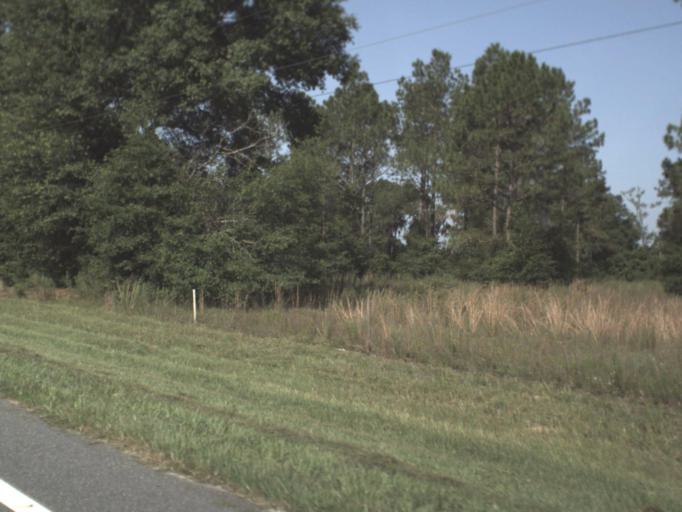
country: US
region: Florida
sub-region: Alachua County
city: High Springs
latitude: 29.8875
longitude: -82.7319
